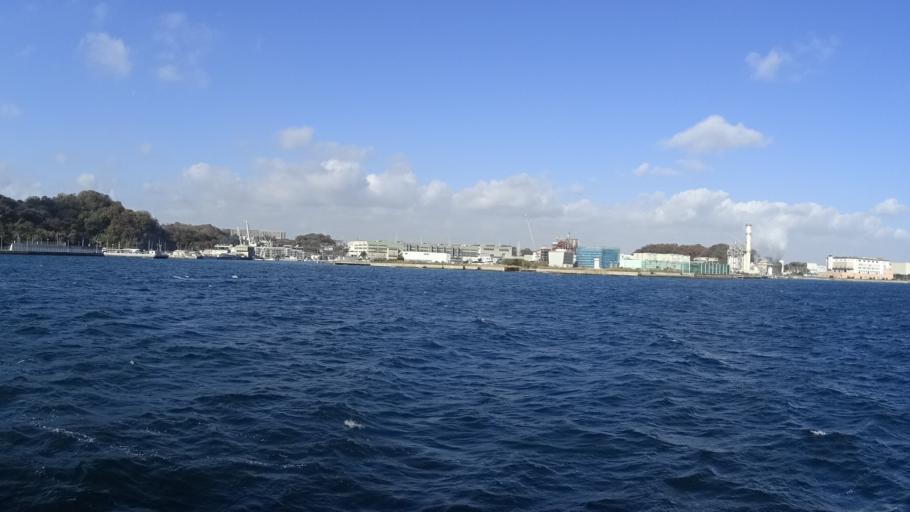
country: JP
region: Kanagawa
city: Yokosuka
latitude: 35.3055
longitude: 139.6465
